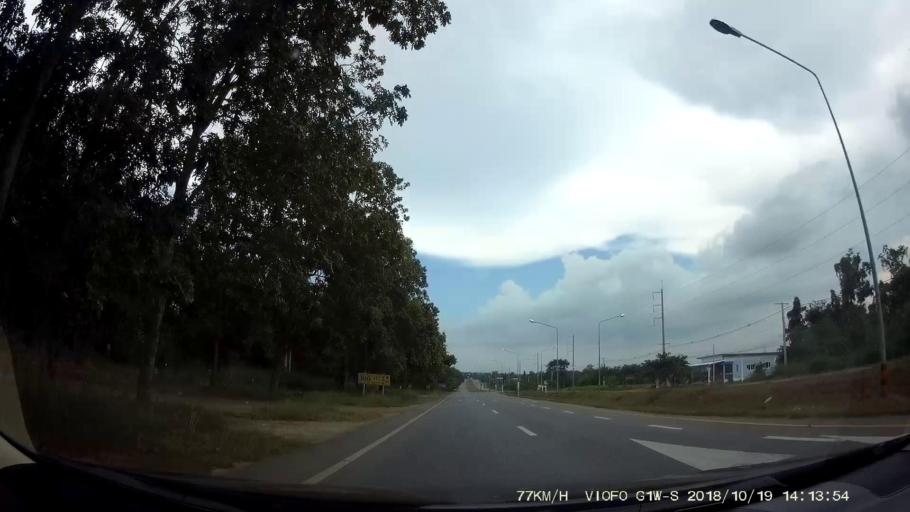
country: TH
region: Chaiyaphum
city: Khon Sawan
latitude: 15.9660
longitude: 102.1829
